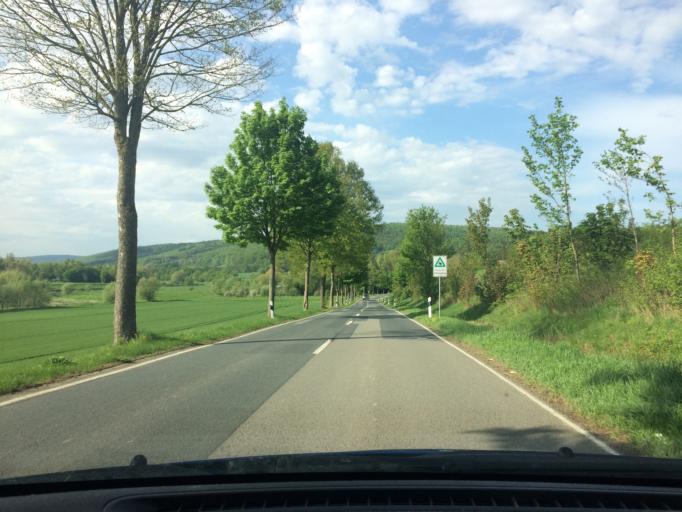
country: DE
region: Lower Saxony
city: Buhren
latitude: 51.5334
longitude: 9.6238
